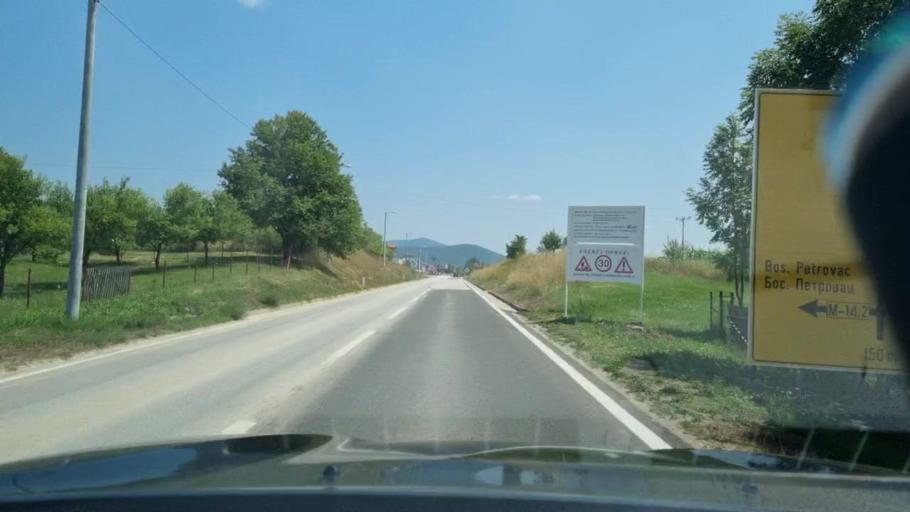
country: BA
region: Federation of Bosnia and Herzegovina
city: Sanica
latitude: 44.5460
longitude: 16.3607
